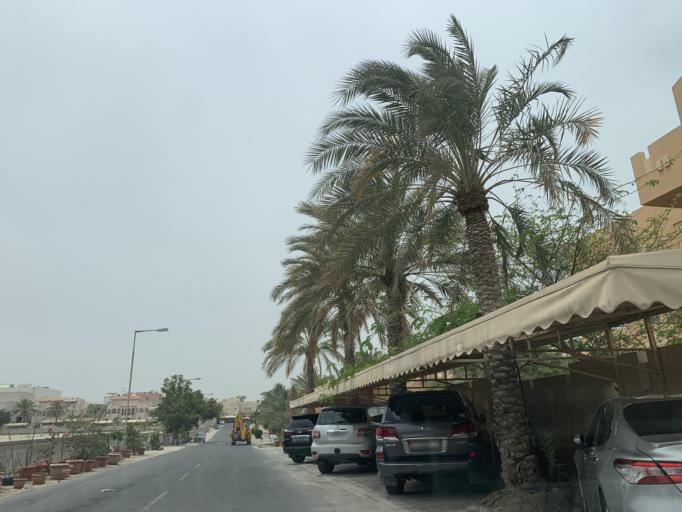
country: BH
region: Northern
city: Ar Rifa'
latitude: 26.1387
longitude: 50.5544
